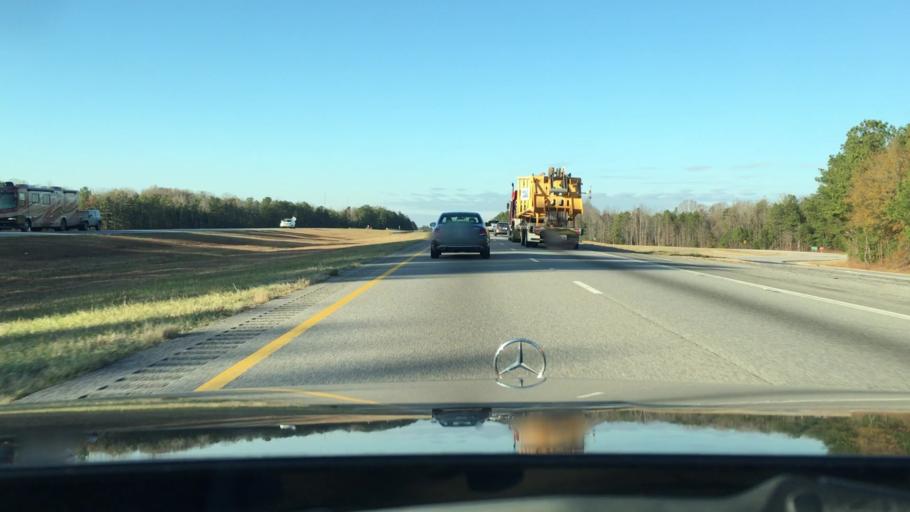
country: US
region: South Carolina
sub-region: Chester County
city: Eureka Mill
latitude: 34.7097
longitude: -81.0307
